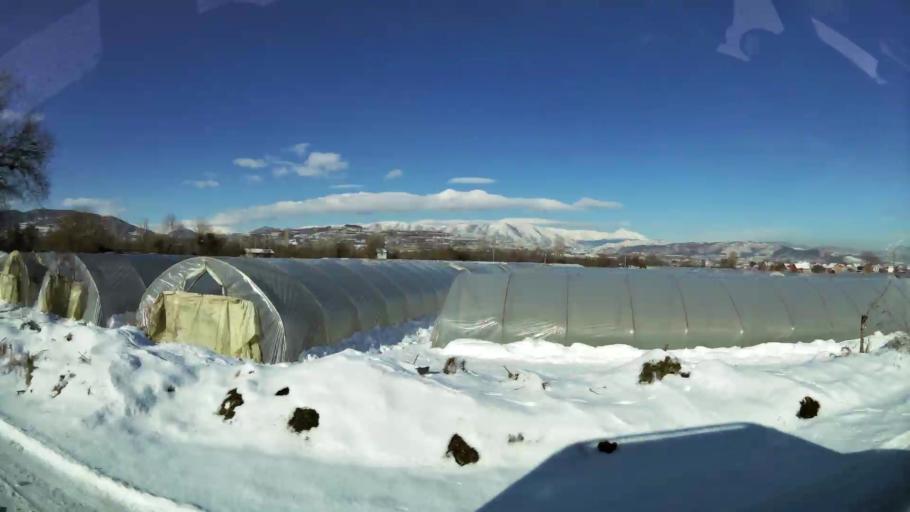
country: MK
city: Grchec
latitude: 41.9848
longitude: 21.3270
